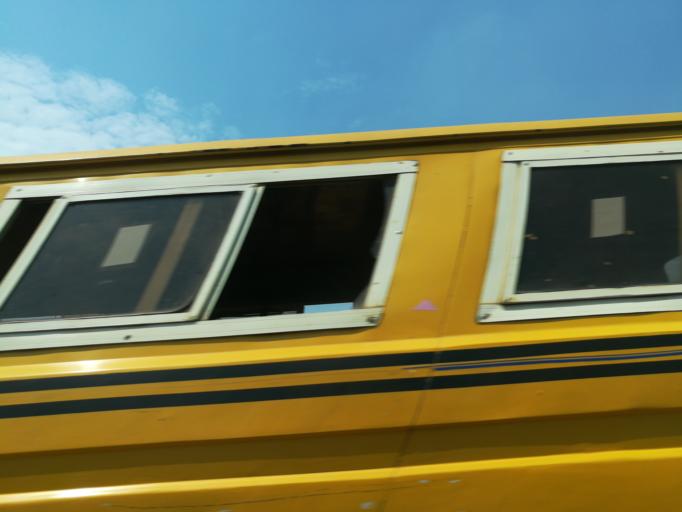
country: NG
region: Lagos
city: Ikorodu
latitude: 6.6618
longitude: 3.4693
